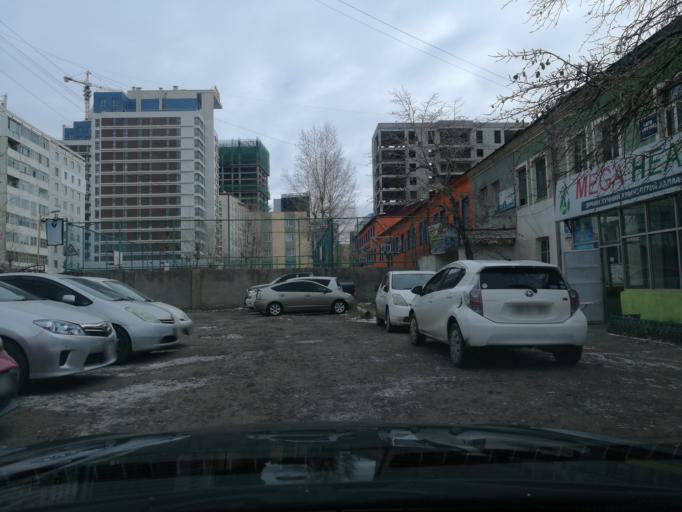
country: MN
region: Ulaanbaatar
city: Ulaanbaatar
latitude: 47.9128
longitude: 106.9098
